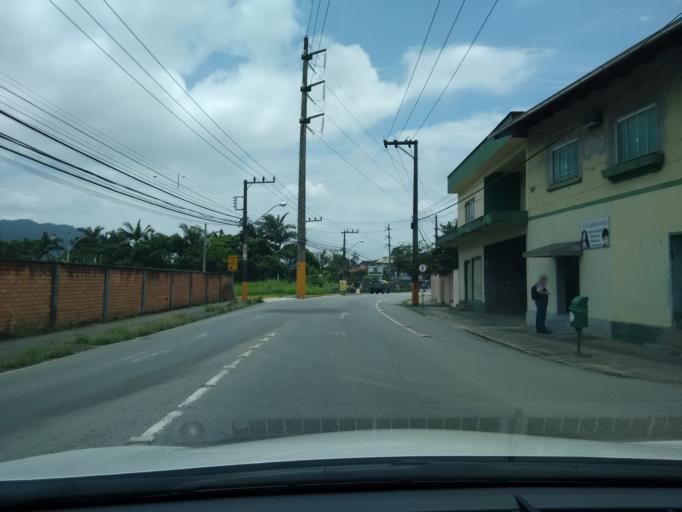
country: BR
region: Santa Catarina
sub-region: Jaragua Do Sul
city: Jaragua do Sul
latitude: -26.4945
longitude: -49.0699
